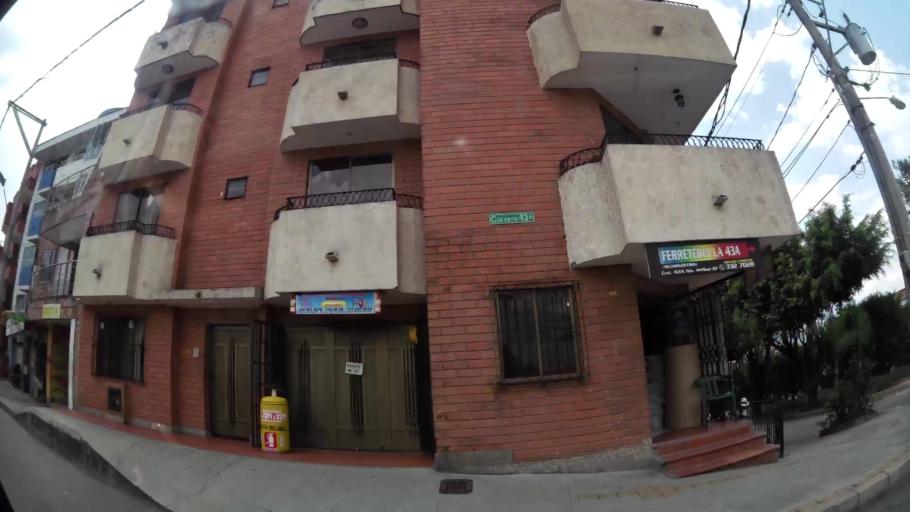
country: CO
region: Antioquia
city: Envigado
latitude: 6.1655
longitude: -75.5942
